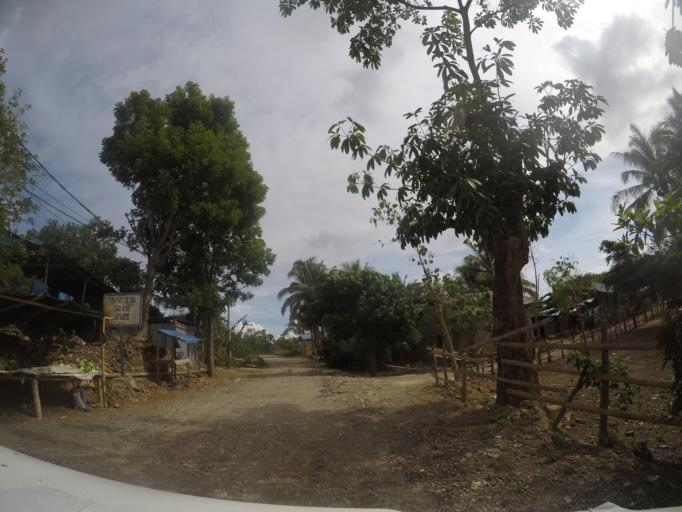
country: TL
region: Baucau
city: Baucau
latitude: -8.4761
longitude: 126.4537
